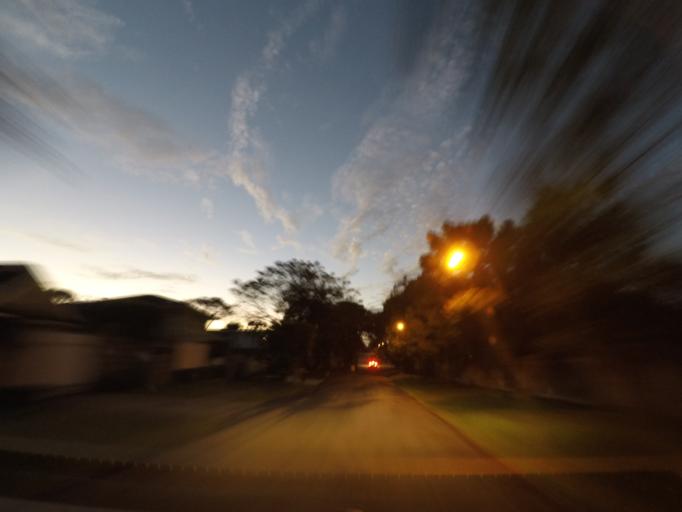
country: BR
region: Parana
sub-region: Curitiba
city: Curitiba
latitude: -25.4223
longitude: -49.2374
